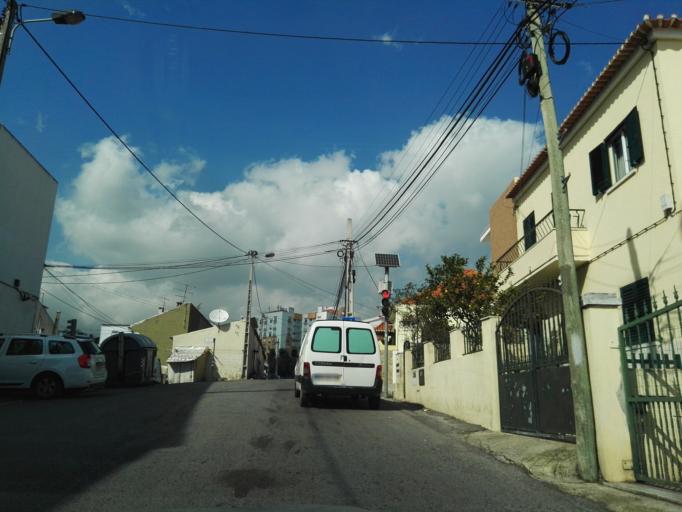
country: PT
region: Lisbon
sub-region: Odivelas
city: Povoa de Santo Adriao
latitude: 38.8027
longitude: -9.1655
